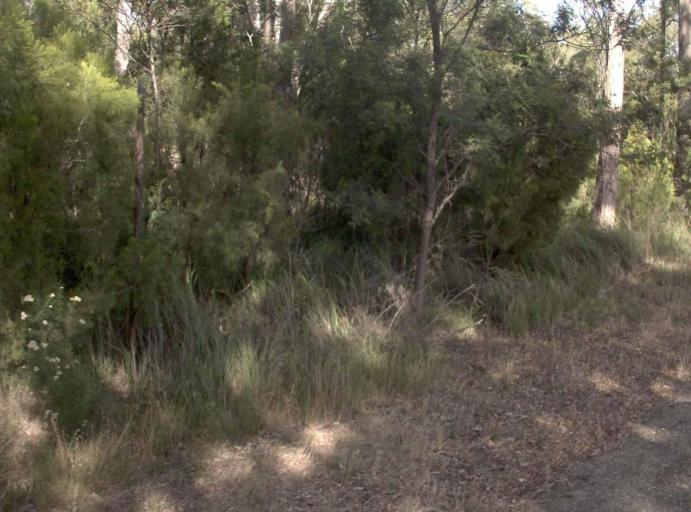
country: AU
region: Victoria
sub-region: East Gippsland
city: Lakes Entrance
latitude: -37.8017
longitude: 147.8364
